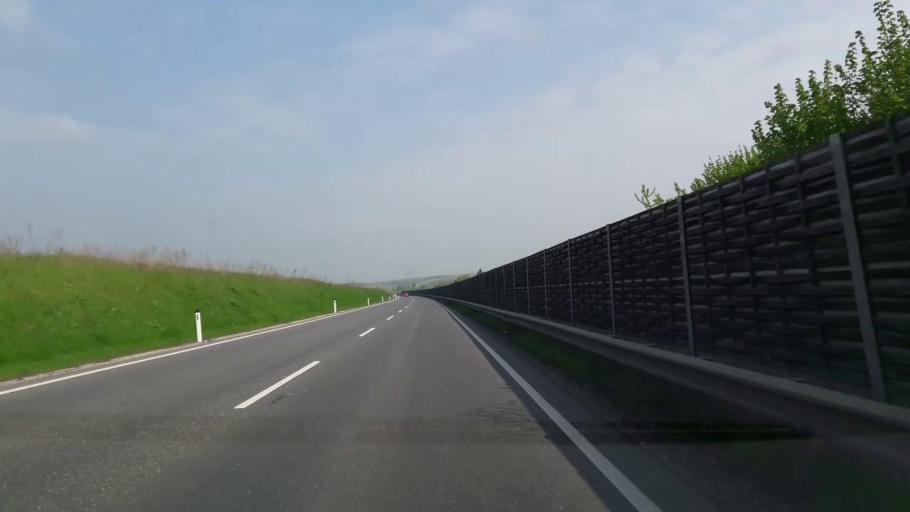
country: AT
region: Lower Austria
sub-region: Politischer Bezirk Hollabrunn
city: Haugsdorf
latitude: 48.7083
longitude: 16.0533
